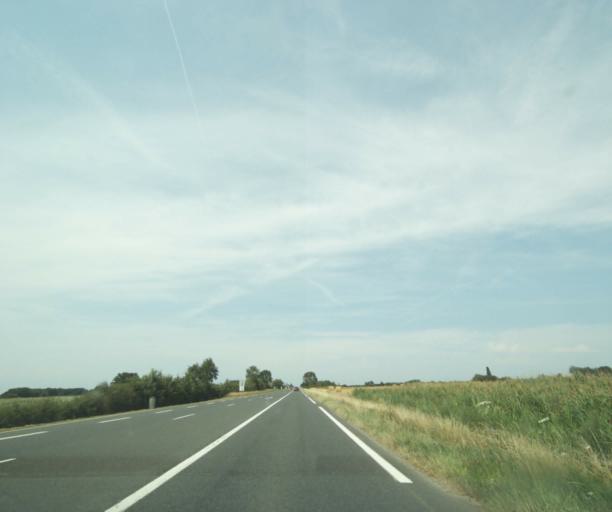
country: FR
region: Centre
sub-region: Departement d'Indre-et-Loire
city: Sorigny
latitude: 47.1864
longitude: 0.6628
